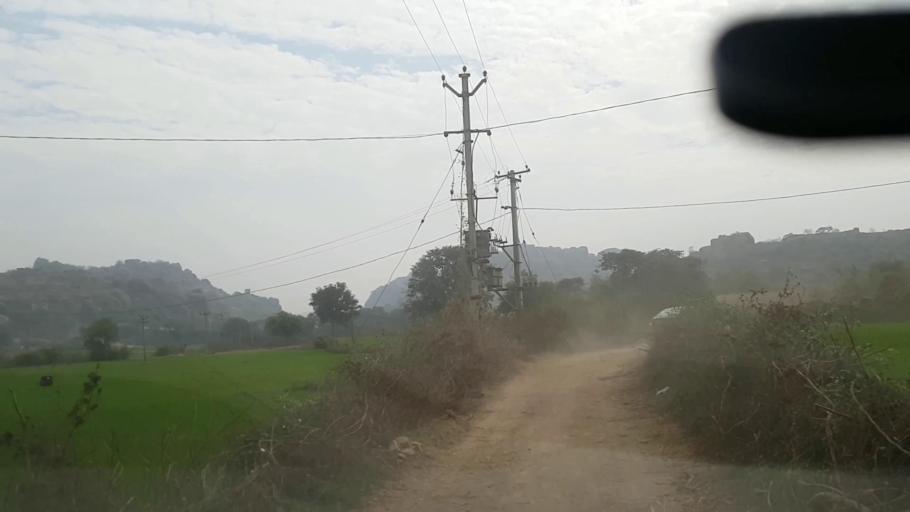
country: IN
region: Telangana
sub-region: Rangareddi
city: Lal Bahadur Nagar
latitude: 17.1814
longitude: 78.7914
